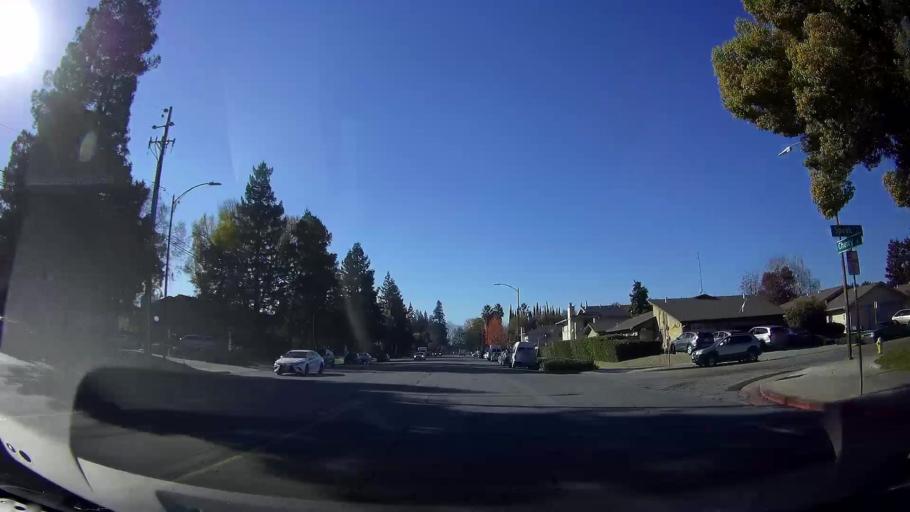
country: US
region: California
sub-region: Santa Clara County
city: Seven Trees
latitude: 37.2586
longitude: -121.8780
